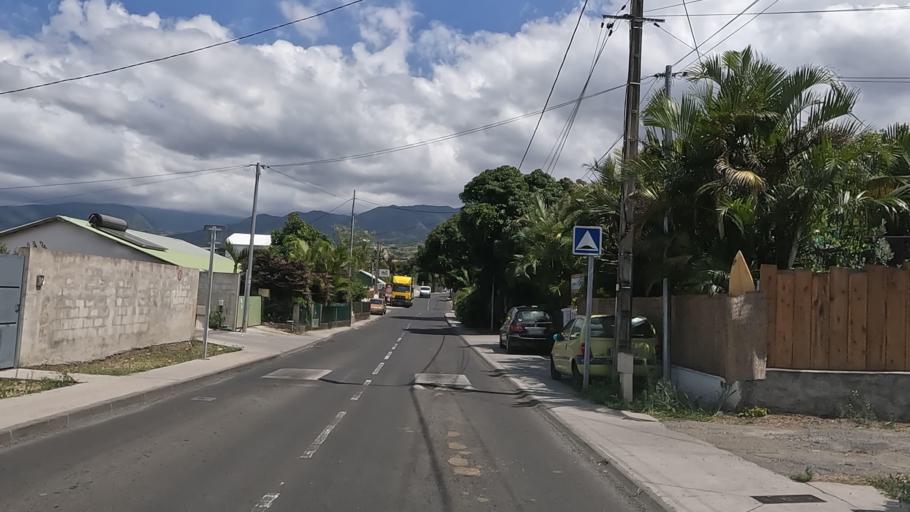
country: RE
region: Reunion
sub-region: Reunion
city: Saint-Louis
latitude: -21.2763
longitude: 55.4496
